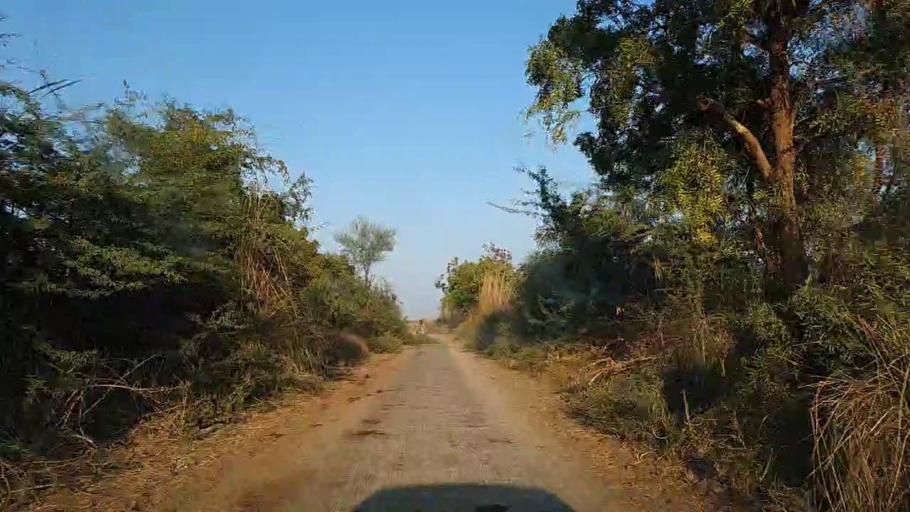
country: PK
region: Sindh
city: Sanghar
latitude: 26.2969
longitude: 68.9872
